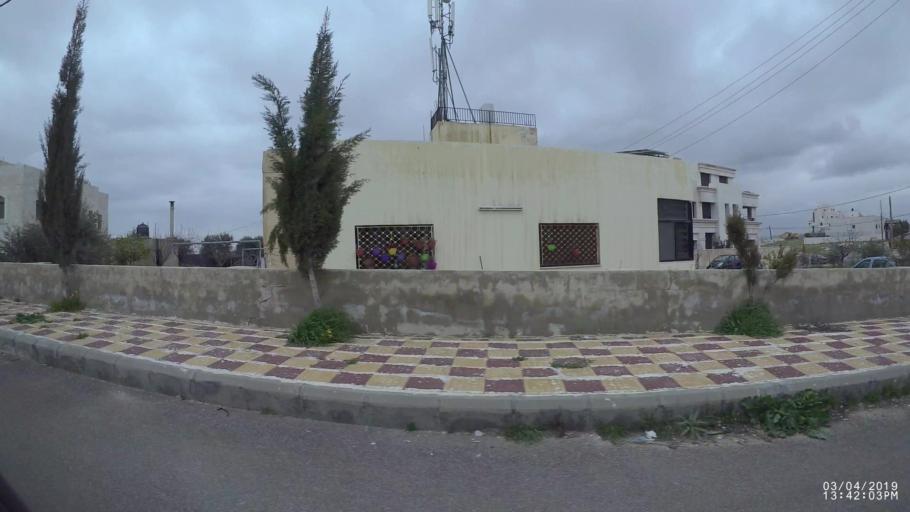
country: JO
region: Amman
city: Wadi as Sir
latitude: 31.9283
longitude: 35.8548
